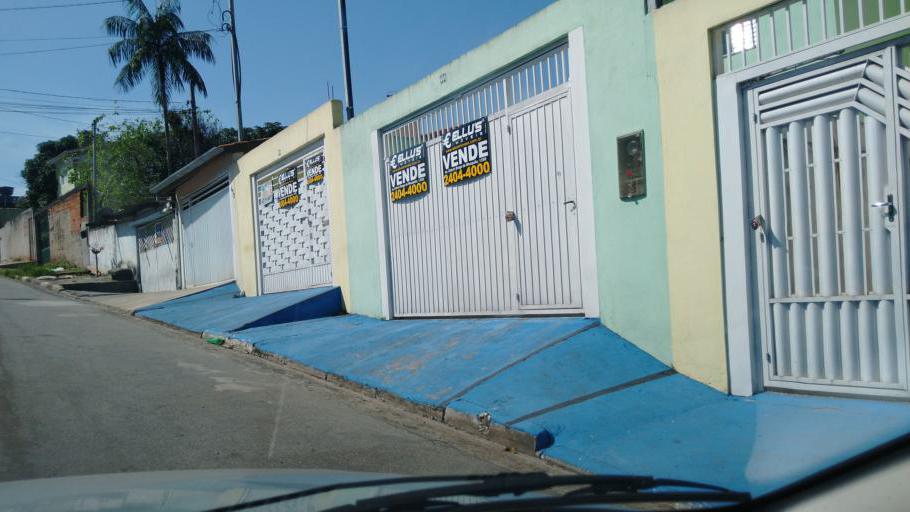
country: BR
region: Sao Paulo
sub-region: Aruja
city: Aruja
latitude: -23.4166
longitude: -46.4034
